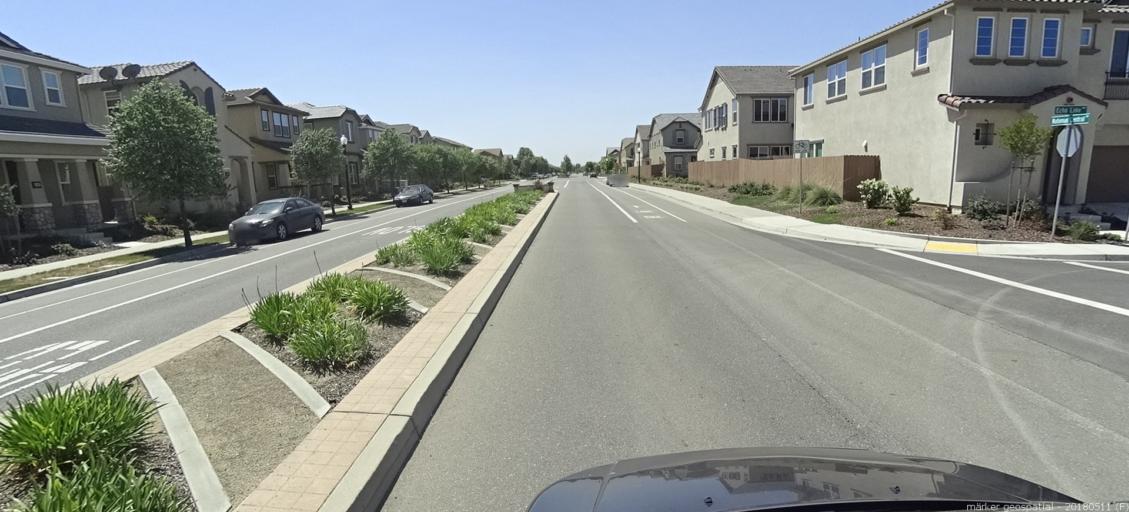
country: US
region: California
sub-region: Yolo County
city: West Sacramento
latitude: 38.6502
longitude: -121.5441
